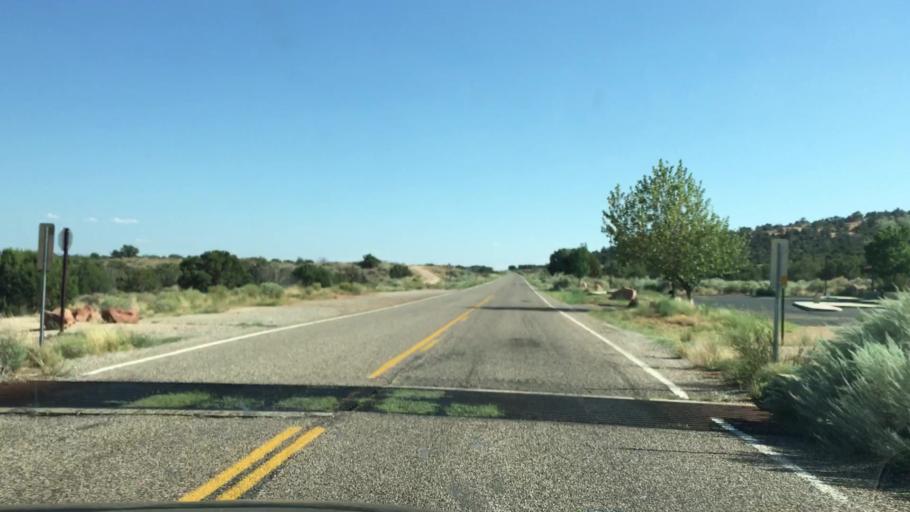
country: US
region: Arizona
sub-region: Coconino County
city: Fredonia
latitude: 36.8811
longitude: -112.7390
